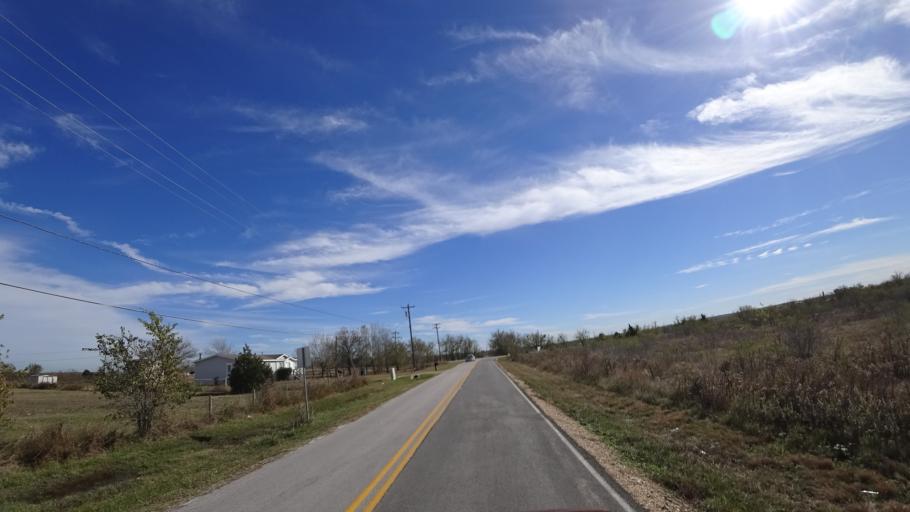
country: US
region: Texas
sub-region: Travis County
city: Onion Creek
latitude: 30.1121
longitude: -97.6967
